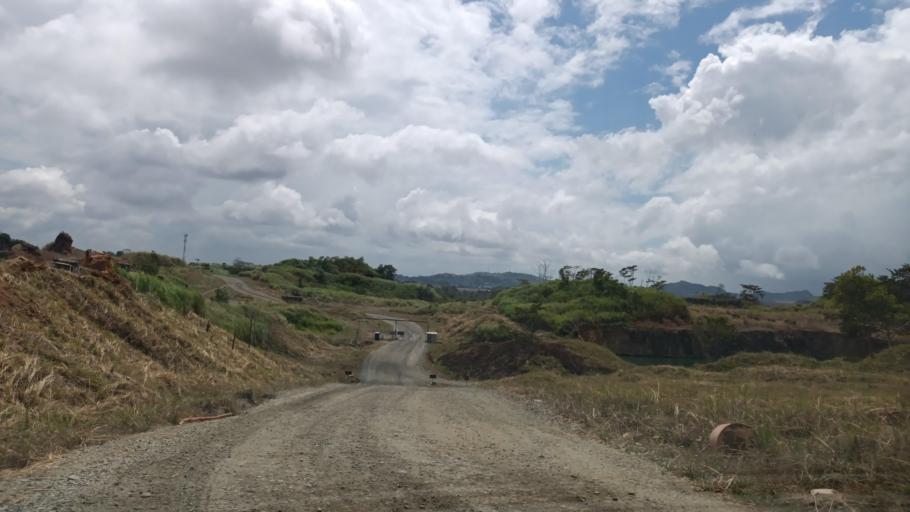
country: PA
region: Panama
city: Las Cumbres
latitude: 9.1087
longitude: -79.4996
